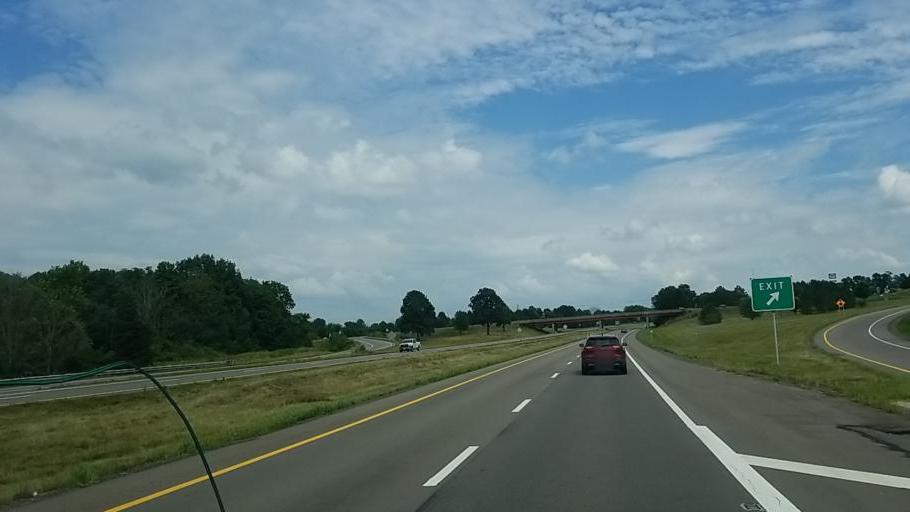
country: US
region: Ohio
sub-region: Ashland County
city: Ashland
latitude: 40.7853
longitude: -82.2670
